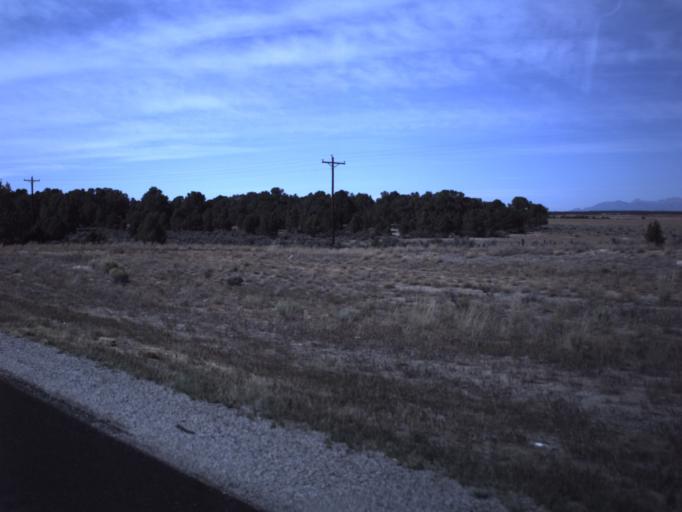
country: US
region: Colorado
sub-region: Dolores County
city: Dove Creek
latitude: 37.8216
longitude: -109.0598
